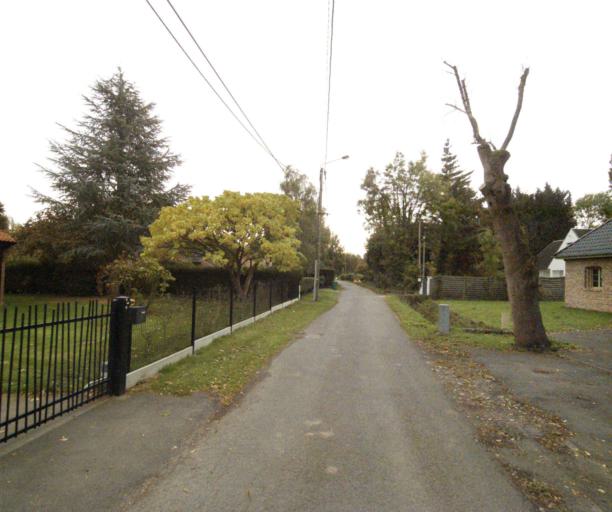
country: FR
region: Nord-Pas-de-Calais
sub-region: Departement du Nord
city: Aubers
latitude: 50.5899
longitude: 2.8125
